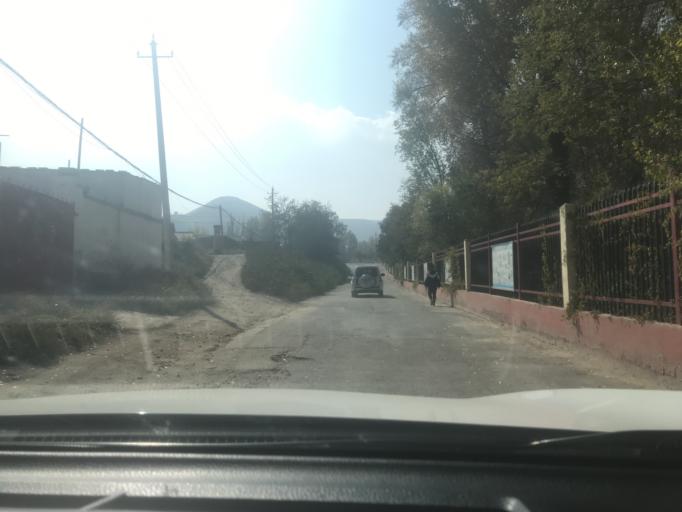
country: CN
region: Gansu Sheng
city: Gulang
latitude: 37.4587
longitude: 102.8888
